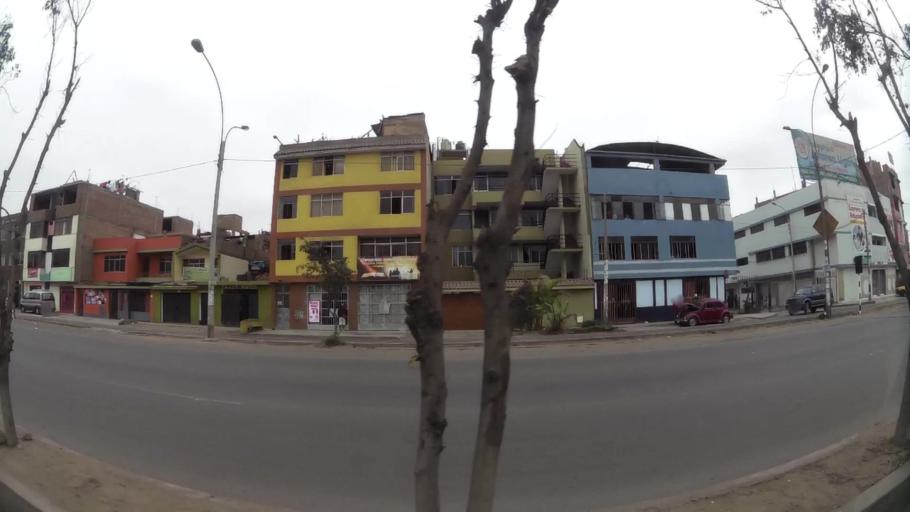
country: PE
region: Lima
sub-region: Lima
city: Independencia
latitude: -11.9783
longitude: -77.0759
